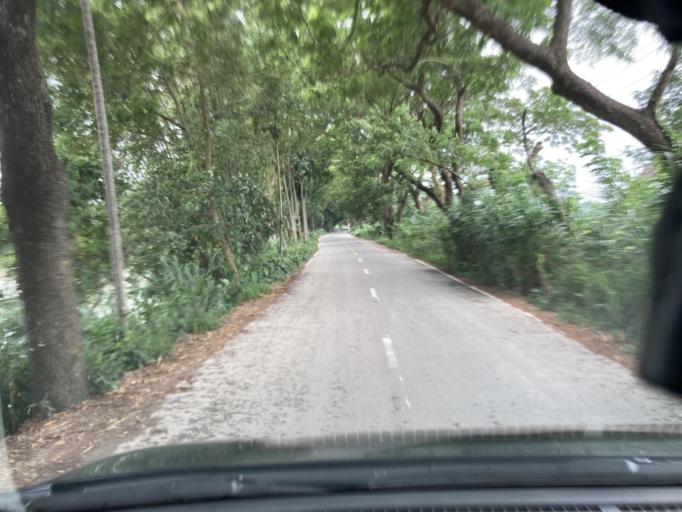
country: BD
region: Dhaka
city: Dohar
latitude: 23.7872
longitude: 90.0636
